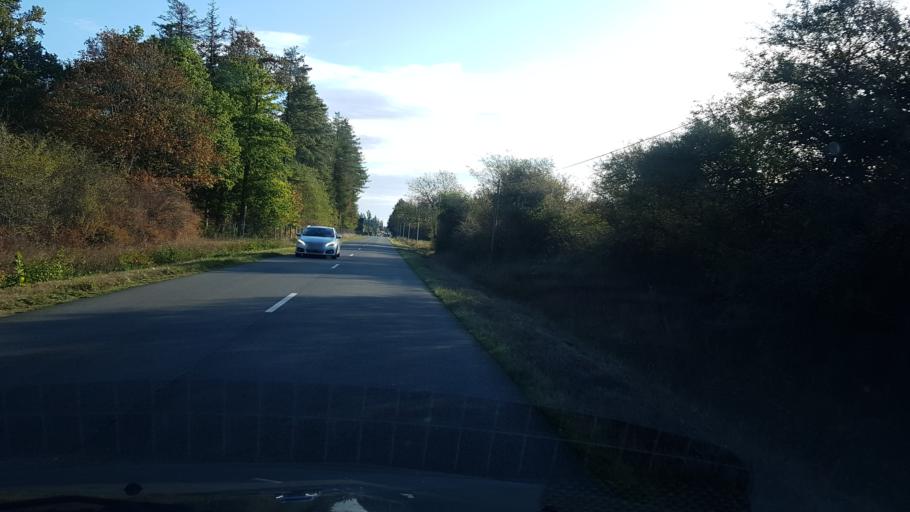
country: FR
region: Centre
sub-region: Departement du Cher
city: Brinon-sur-Sauldre
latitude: 47.6680
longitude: 2.2432
